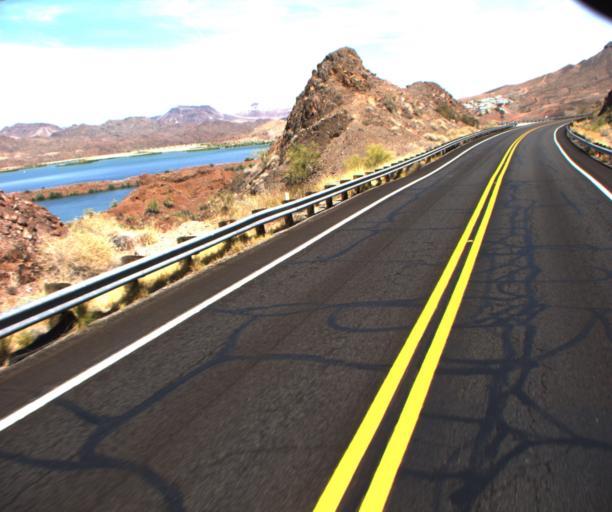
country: US
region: Arizona
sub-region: La Paz County
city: Cienega Springs
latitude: 34.2914
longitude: -114.1175
